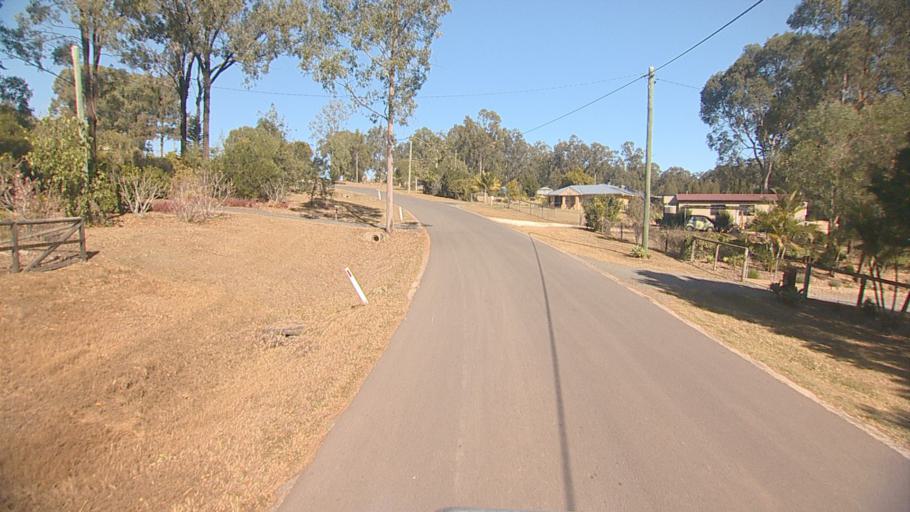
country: AU
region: Queensland
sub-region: Logan
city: Cedar Vale
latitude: -27.8785
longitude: 153.0068
